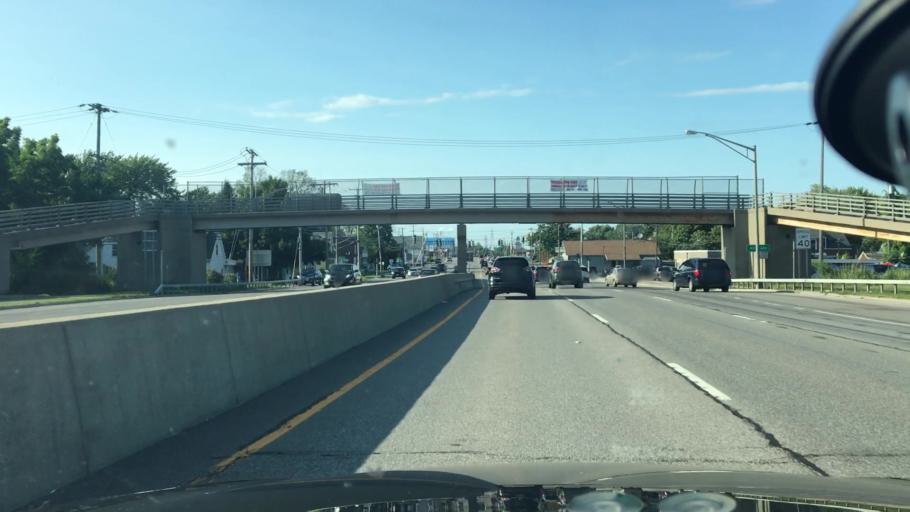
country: US
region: New York
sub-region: Erie County
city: Blasdell
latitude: 42.7931
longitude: -78.8468
